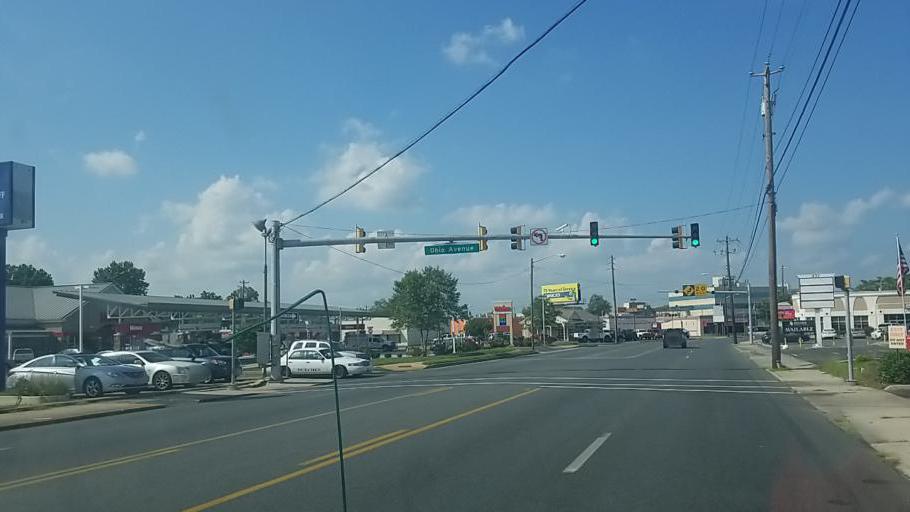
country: US
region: Maryland
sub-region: Wicomico County
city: Salisbury
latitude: 38.3574
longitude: -75.5999
